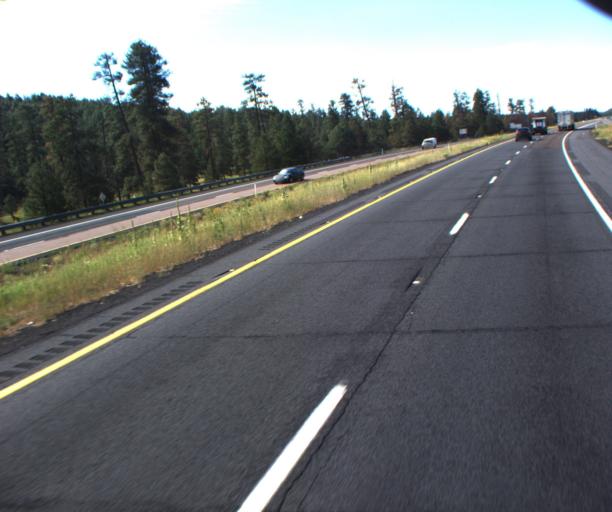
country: US
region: Arizona
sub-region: Coconino County
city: Mountainaire
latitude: 35.0177
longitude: -111.6848
